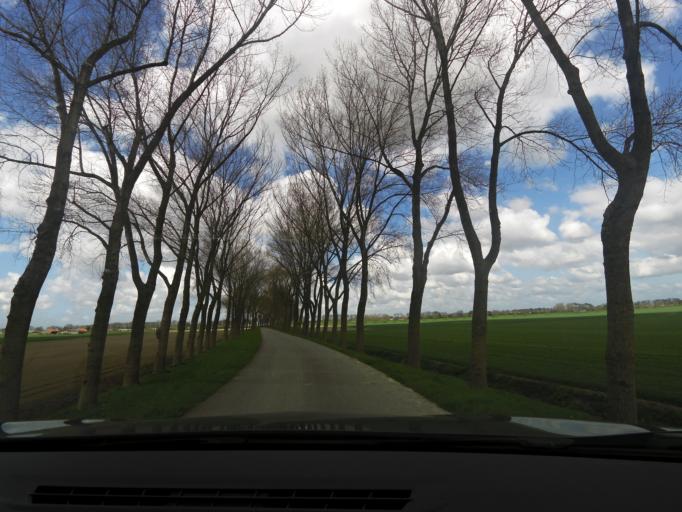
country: NL
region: South Holland
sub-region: Gemeente Albrandswaard
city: Rhoon
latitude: 51.8430
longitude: 4.4500
